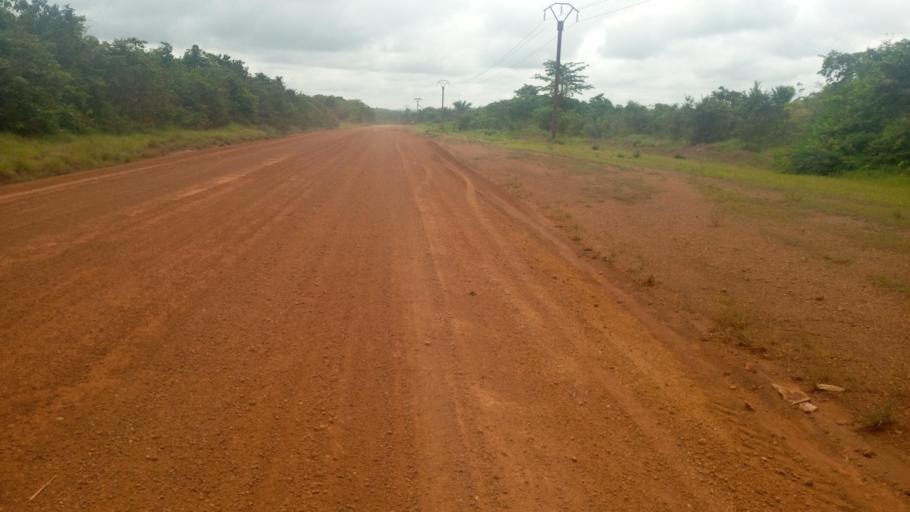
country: SL
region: Southern Province
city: Mogbwemo
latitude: 7.7231
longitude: -12.2839
